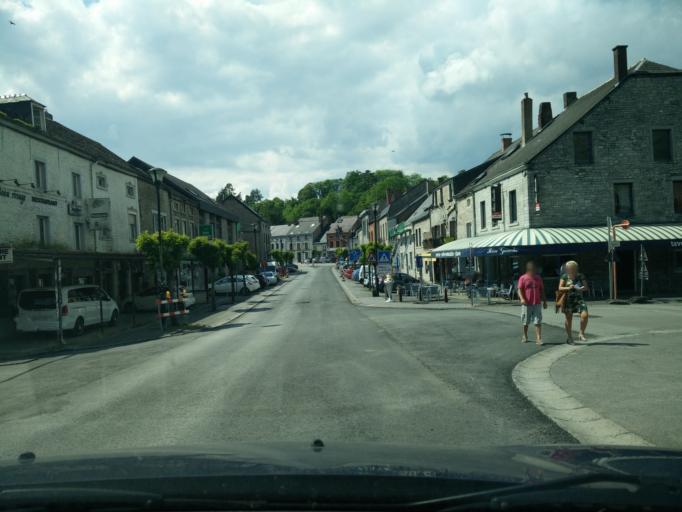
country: BE
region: Wallonia
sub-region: Province de Namur
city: Couvin
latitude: 50.0747
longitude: 4.5485
